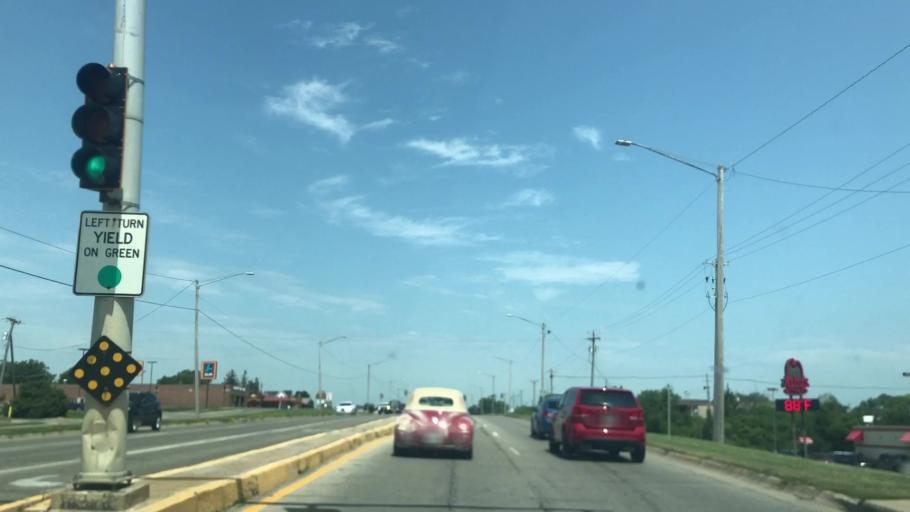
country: US
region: Iowa
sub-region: Marshall County
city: Marshalltown
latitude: 42.0157
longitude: -92.9123
